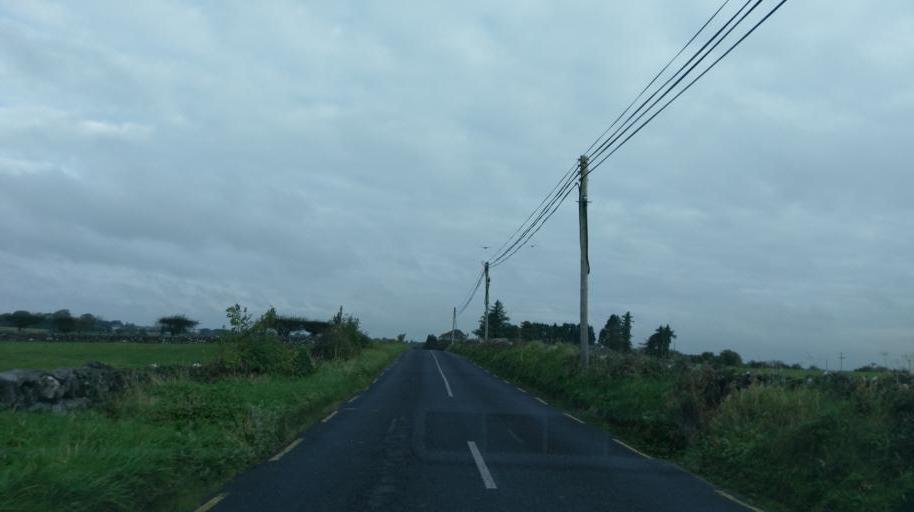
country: IE
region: Connaught
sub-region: County Galway
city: Athenry
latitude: 53.3565
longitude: -8.7052
